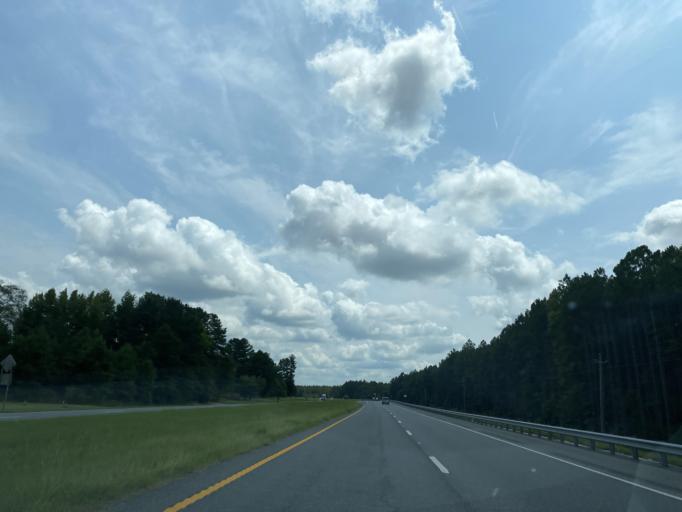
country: US
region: Georgia
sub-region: Ware County
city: Deenwood
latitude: 31.3344
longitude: -82.4639
